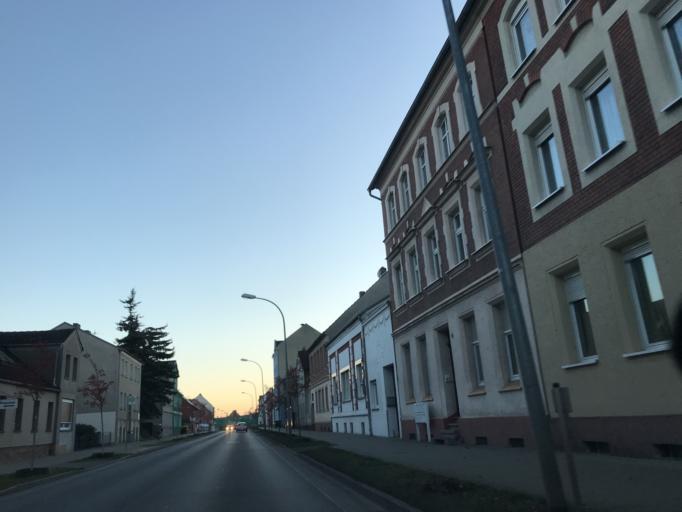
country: DE
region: Brandenburg
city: Rathenow
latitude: 52.5989
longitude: 12.3377
